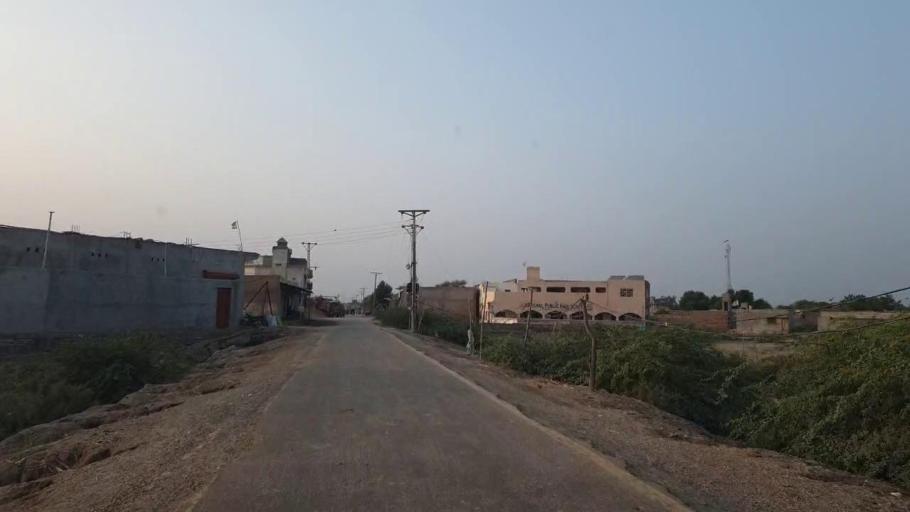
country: PK
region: Sindh
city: Tando Ghulam Ali
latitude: 25.1435
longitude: 68.9580
